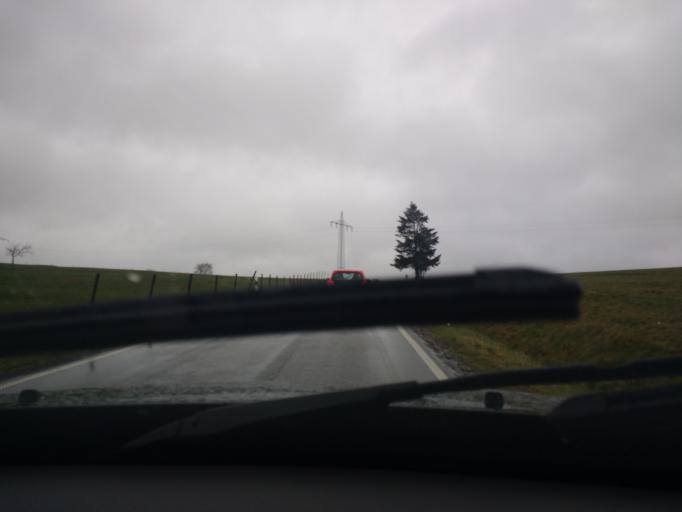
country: DE
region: Rheinland-Pfalz
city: Franzenheim
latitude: 49.6852
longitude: 6.6945
